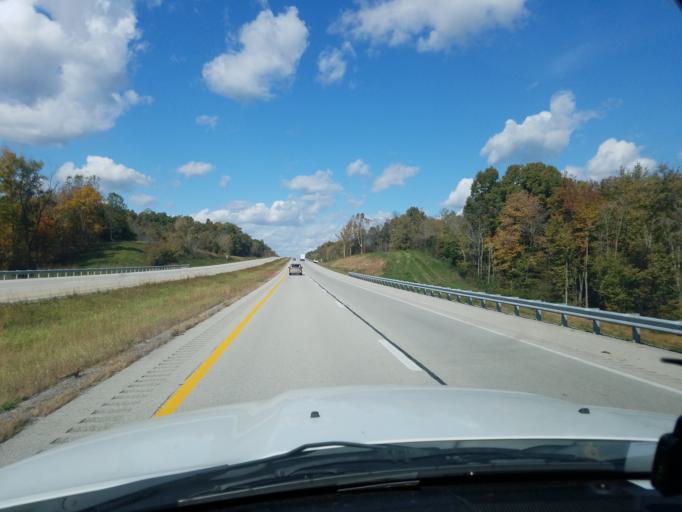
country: US
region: Kentucky
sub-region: Ohio County
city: Hartford
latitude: 37.5606
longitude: -86.9428
